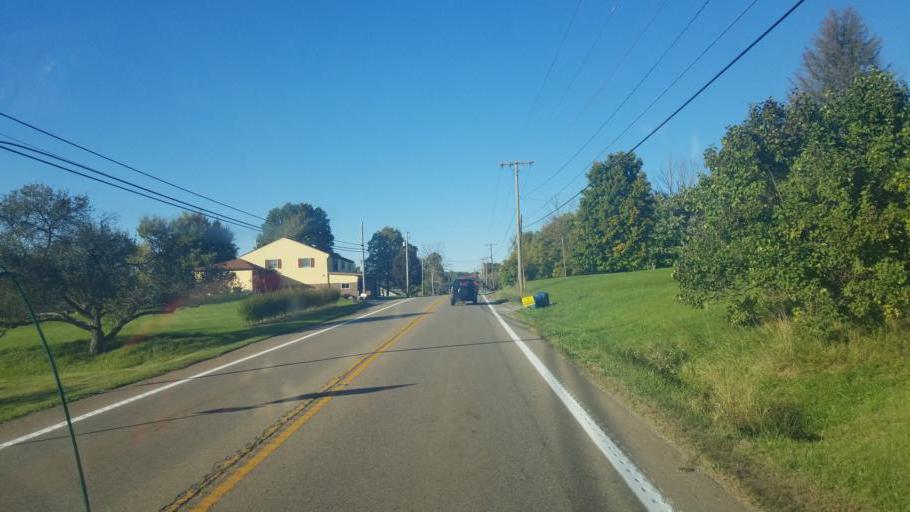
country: US
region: Ohio
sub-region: Columbiana County
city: New Waterford
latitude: 40.8170
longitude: -80.6362
